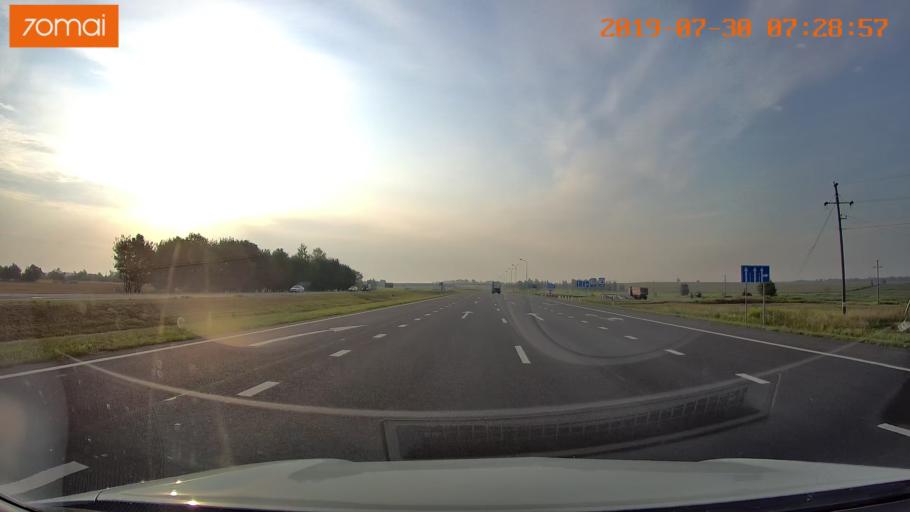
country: RU
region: Kaliningrad
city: Gvardeysk
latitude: 54.6744
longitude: 20.9284
